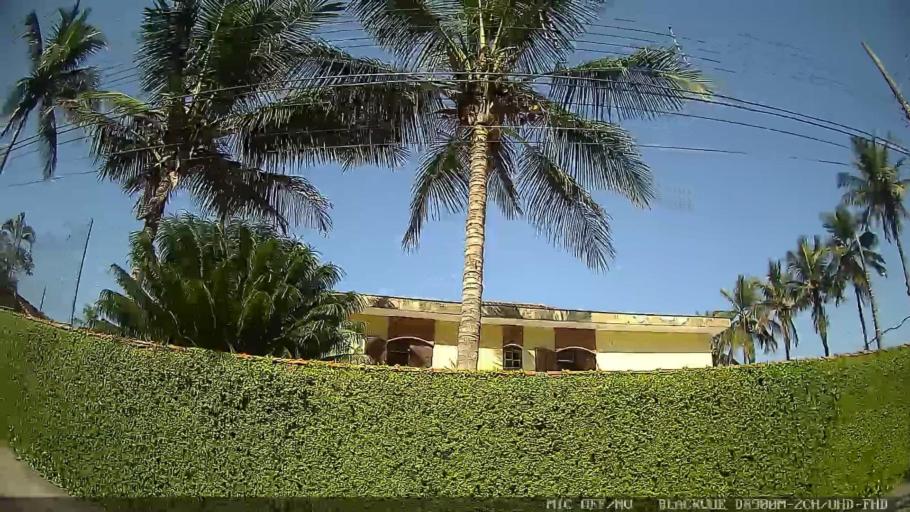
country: BR
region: Sao Paulo
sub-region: Guaruja
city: Guaruja
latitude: -24.0137
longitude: -46.2896
